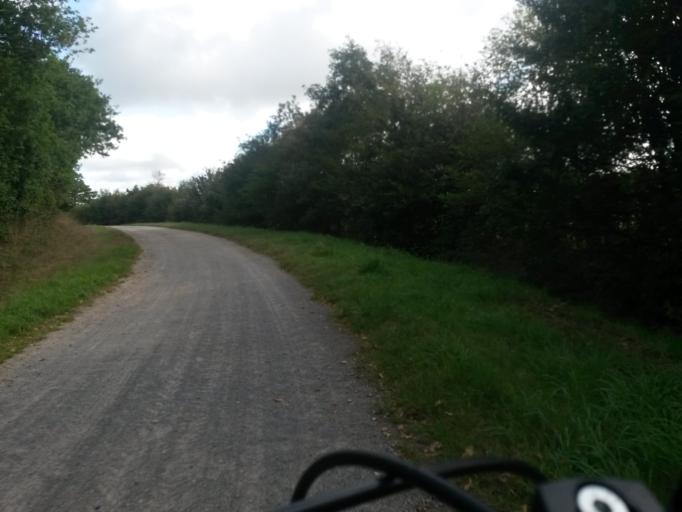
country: FR
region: Pays de la Loire
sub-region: Departement de la Loire-Atlantique
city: Guerande
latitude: 47.3434
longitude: -2.3840
